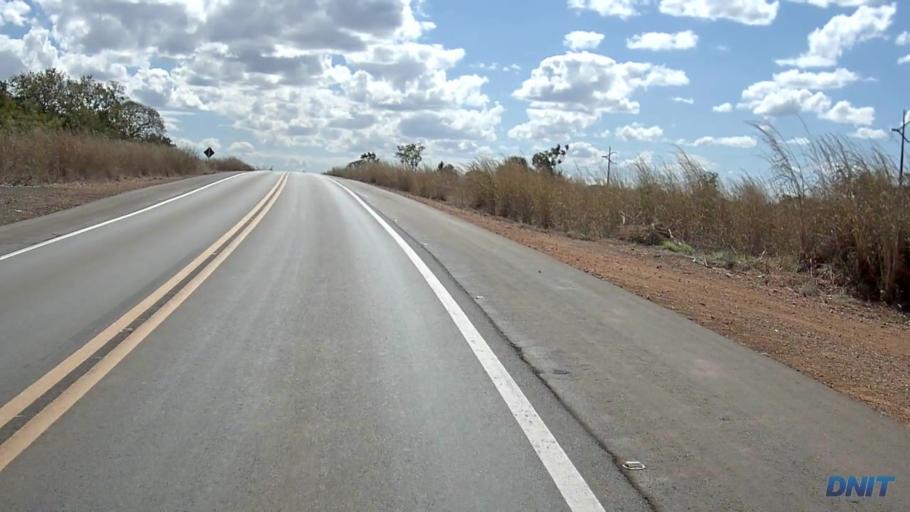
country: BR
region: Goias
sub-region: Uruacu
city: Uruacu
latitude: -14.7342
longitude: -49.0699
